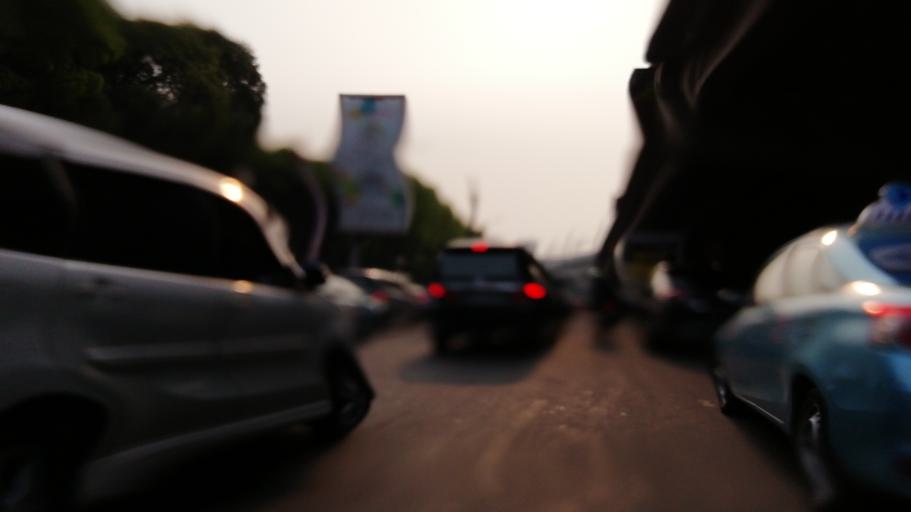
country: ID
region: West Java
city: Pamulang
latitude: -6.2925
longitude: 106.7965
